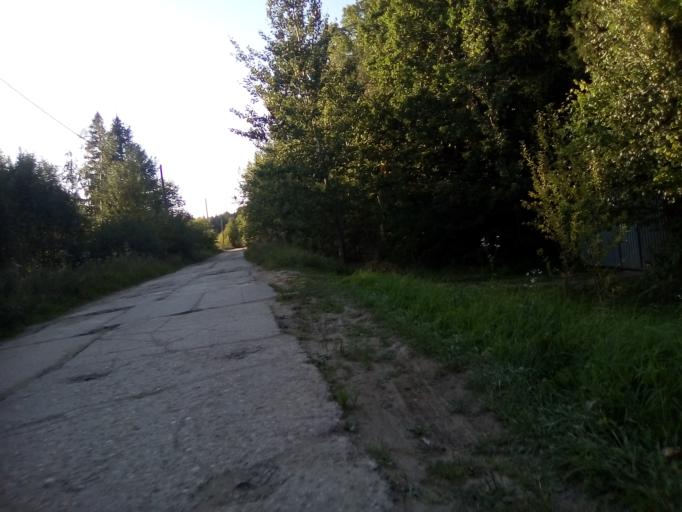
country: RU
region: Moskovskaya
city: Aprelevka
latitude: 55.5669
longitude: 37.0692
